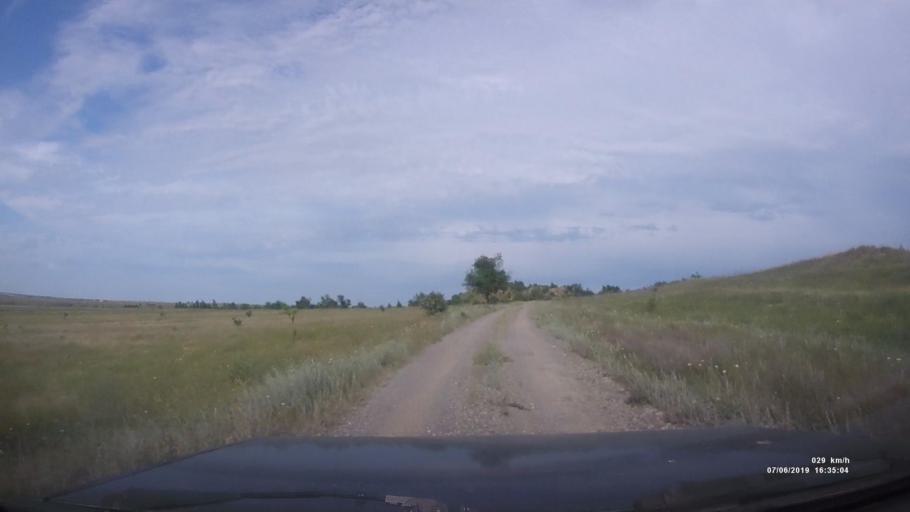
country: RU
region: Rostov
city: Staraya Stanitsa
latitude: 48.2512
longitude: 40.3457
